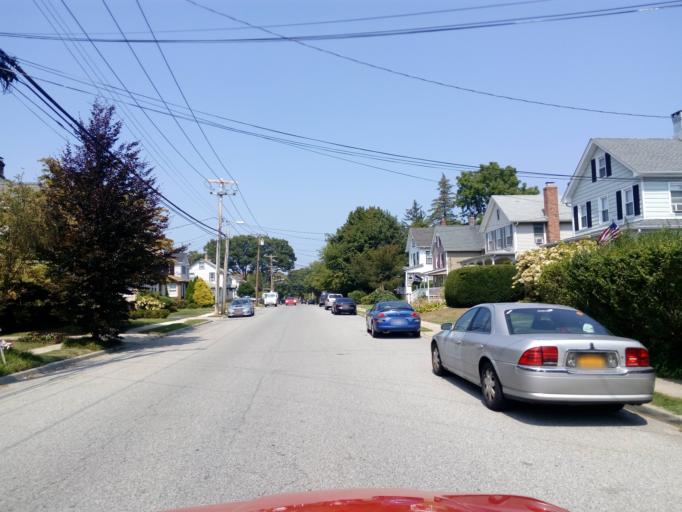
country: US
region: New York
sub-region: Nassau County
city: Glen Cove
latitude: 40.8700
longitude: -73.6350
